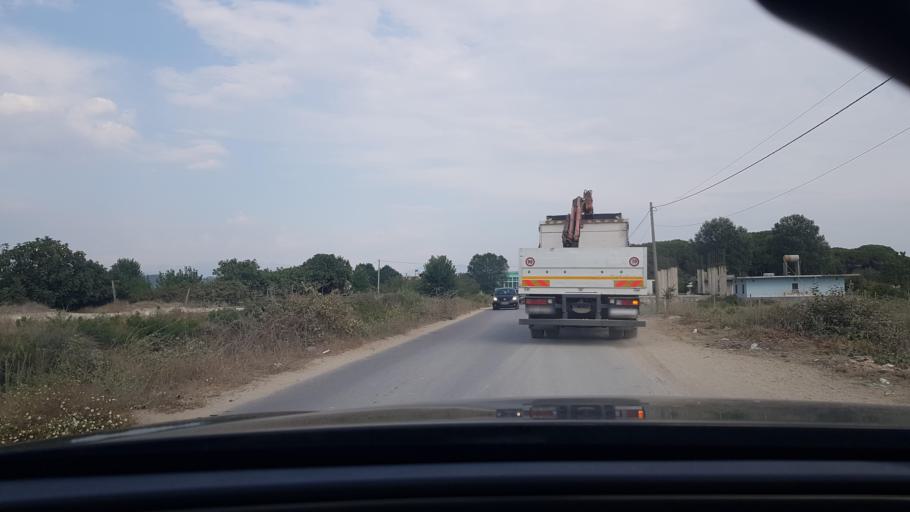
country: AL
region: Durres
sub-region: Rrethi i Durresit
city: Katundi i Ri
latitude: 41.4869
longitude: 19.5142
